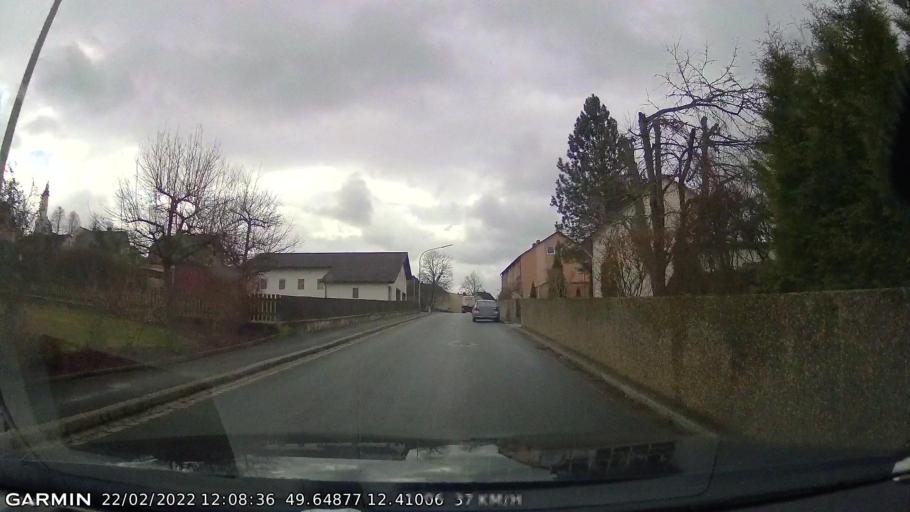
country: DE
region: Bavaria
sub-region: Upper Palatinate
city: Pleystein
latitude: 49.6487
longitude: 12.4100
